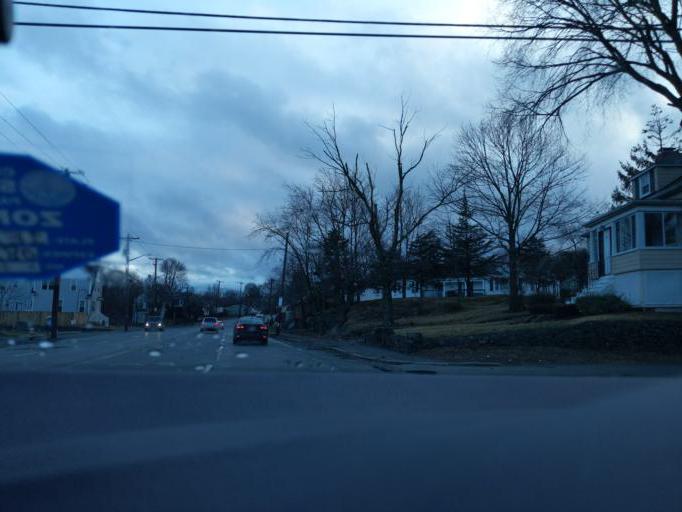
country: US
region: Massachusetts
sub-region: Essex County
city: Salem
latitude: 42.5108
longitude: -70.9098
